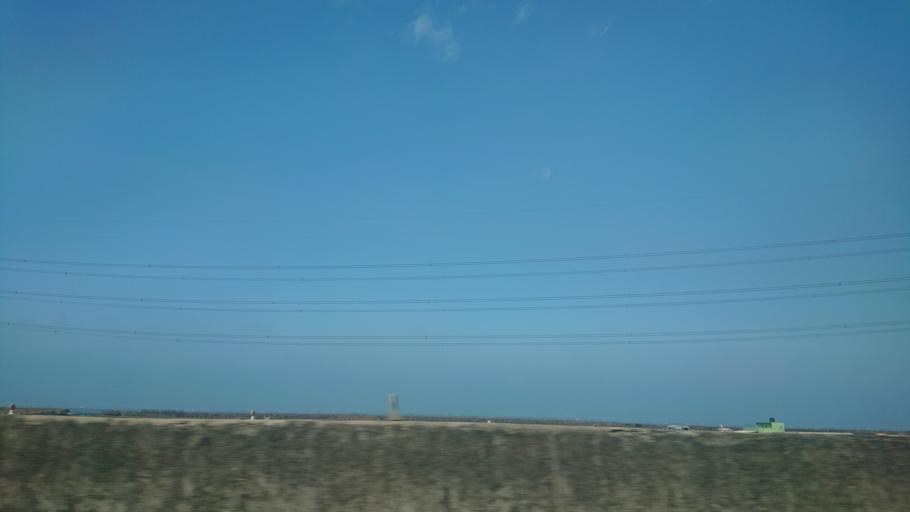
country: TW
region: Taiwan
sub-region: Changhua
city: Chang-hua
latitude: 24.1690
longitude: 120.4708
